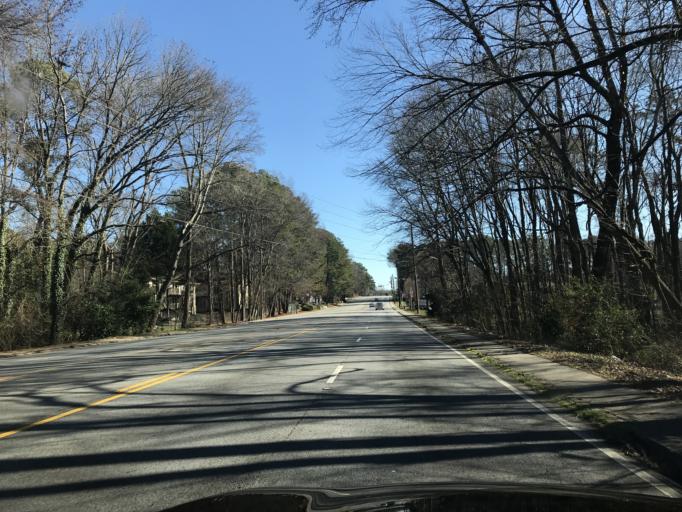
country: US
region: Georgia
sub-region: Clayton County
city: Morrow
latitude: 33.5727
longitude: -84.3646
